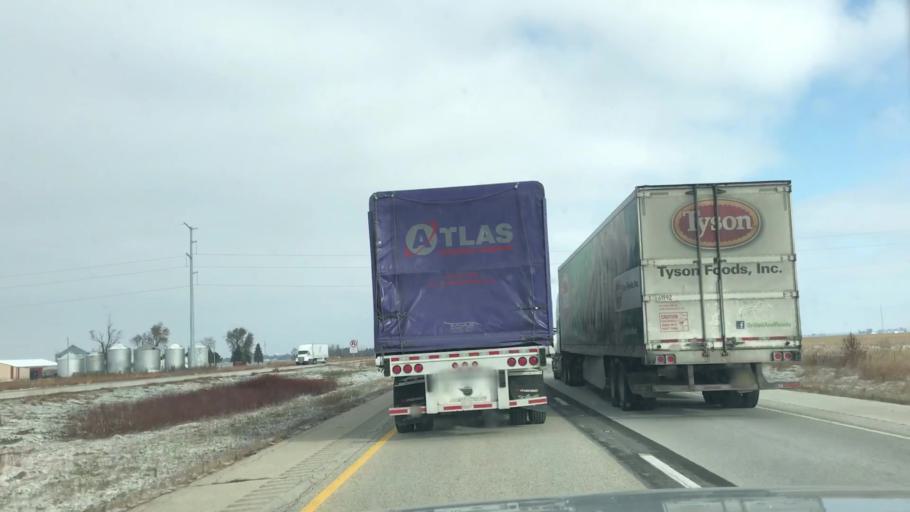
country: US
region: Illinois
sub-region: Sangamon County
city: Divernon
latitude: 39.5290
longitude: -89.6455
